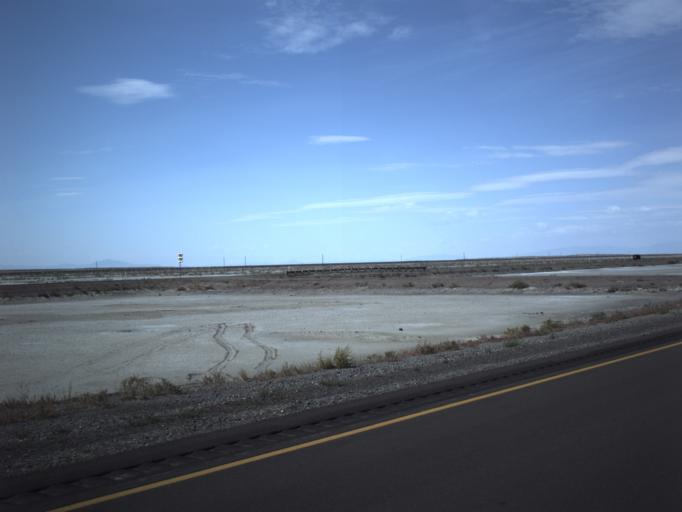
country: US
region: Utah
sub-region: Tooele County
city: Wendover
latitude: 40.7282
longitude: -113.3117
